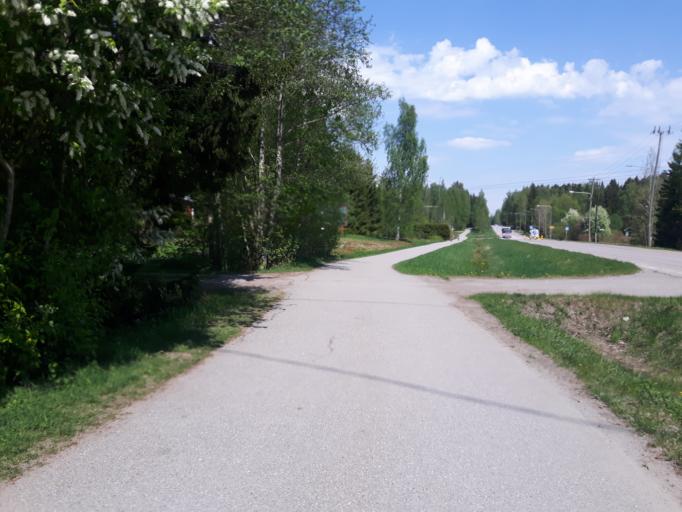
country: FI
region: Uusimaa
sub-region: Porvoo
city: Porvoo
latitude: 60.3836
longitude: 25.6233
